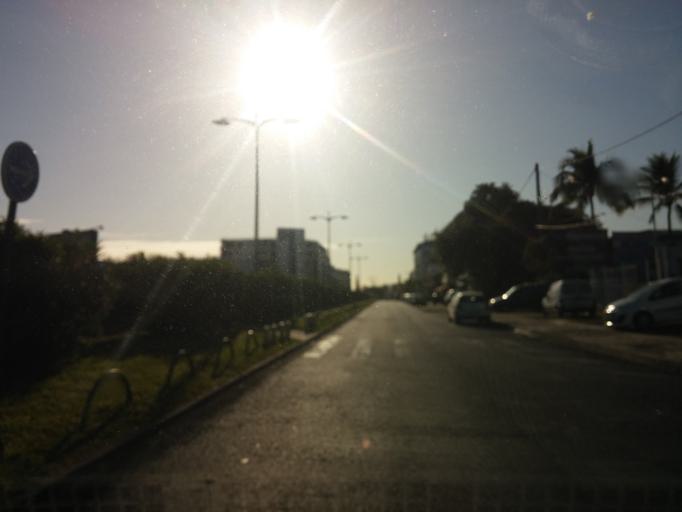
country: RE
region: Reunion
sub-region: Reunion
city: Le Port
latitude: -20.9332
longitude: 55.2929
